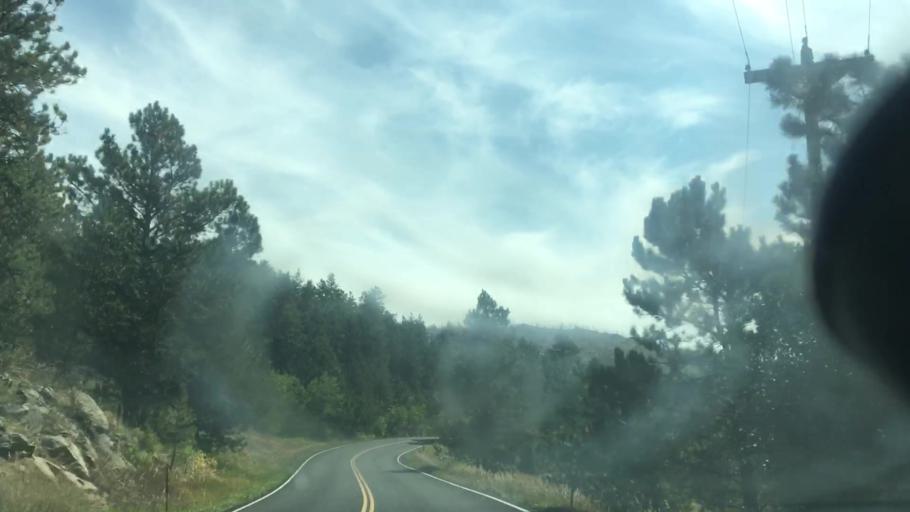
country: US
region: Colorado
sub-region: Larimer County
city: Laporte
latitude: 40.6053
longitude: -105.3464
